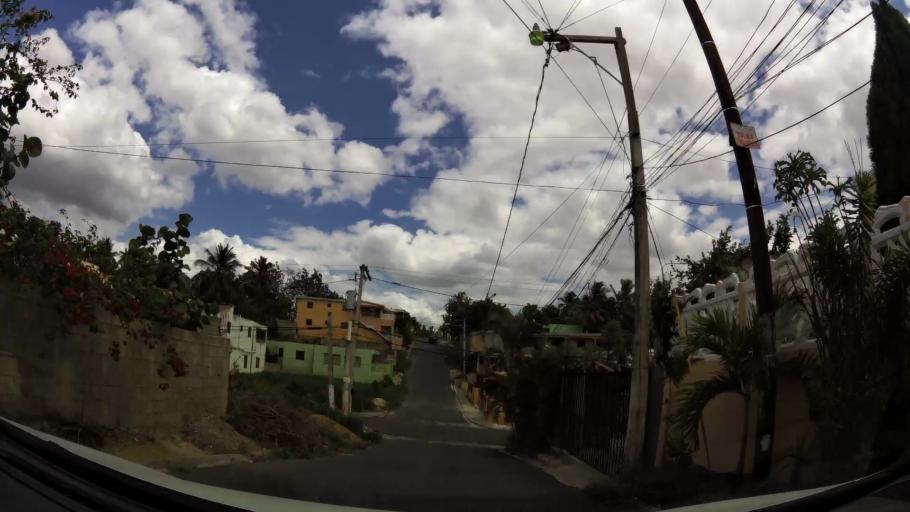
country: DO
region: Nacional
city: Ensanche Luperon
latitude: 18.5259
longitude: -69.9072
